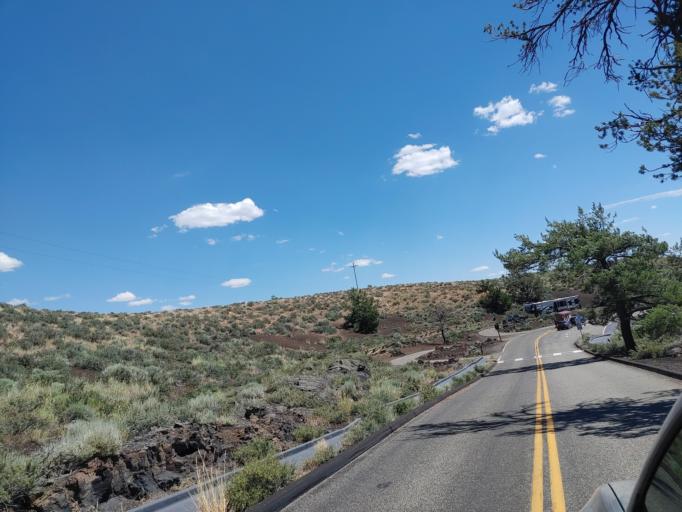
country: US
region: Idaho
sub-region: Butte County
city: Arco
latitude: 43.4617
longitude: -113.5578
